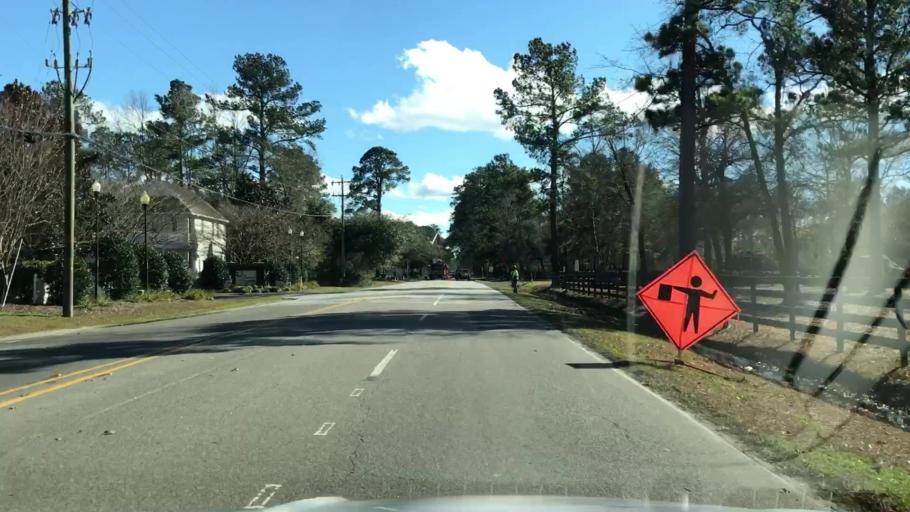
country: US
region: South Carolina
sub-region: Dorchester County
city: Summerville
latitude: 33.0344
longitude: -80.2465
